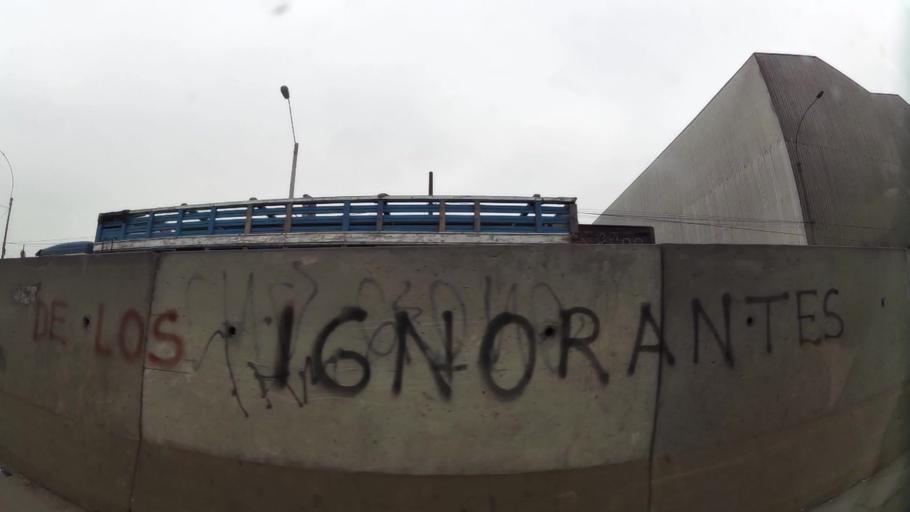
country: PE
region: Lima
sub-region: Lima
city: San Luis
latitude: -12.0625
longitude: -76.9758
